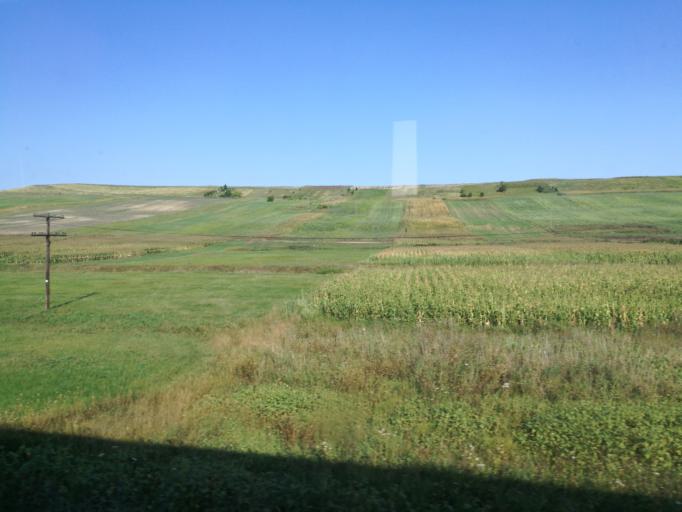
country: RO
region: Vaslui
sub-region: Comuna Rebricea
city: Rebricea
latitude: 46.8646
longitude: 27.5640
